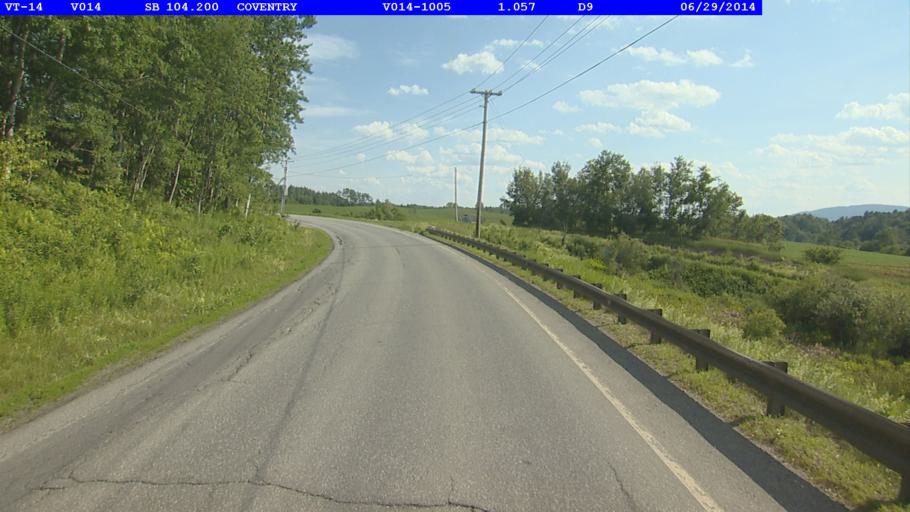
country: US
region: Vermont
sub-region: Orleans County
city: Newport
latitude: 44.8793
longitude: -72.2653
